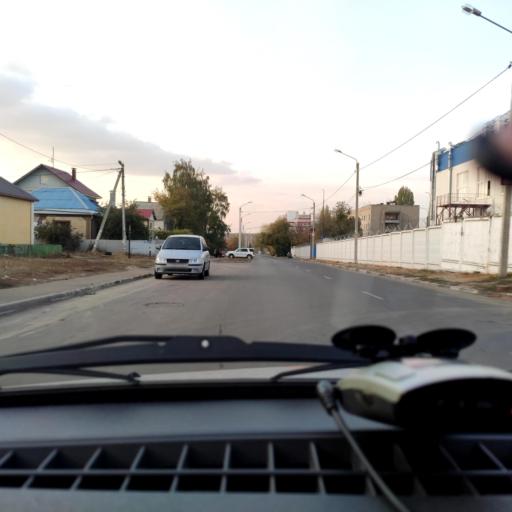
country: RU
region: Voronezj
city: Pridonskoy
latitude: 51.6593
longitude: 39.1265
